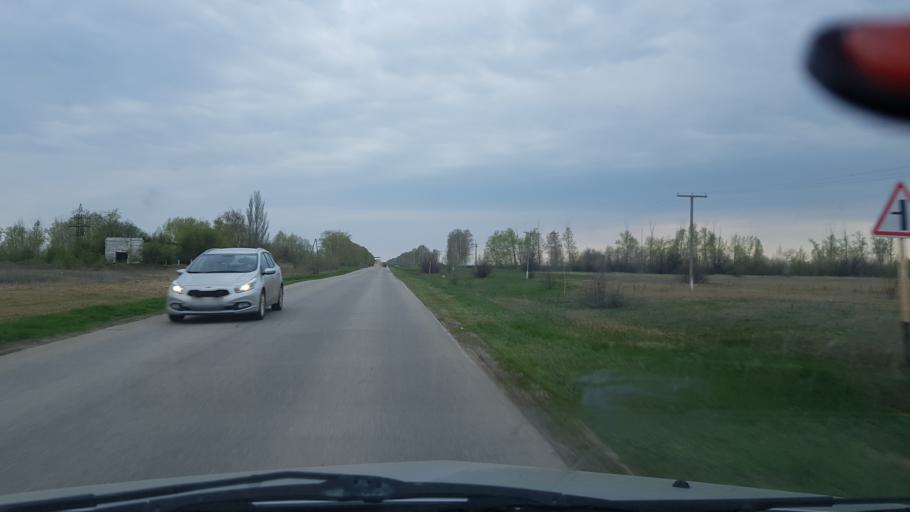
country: RU
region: Samara
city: Tol'yatti
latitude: 53.6578
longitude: 49.2451
